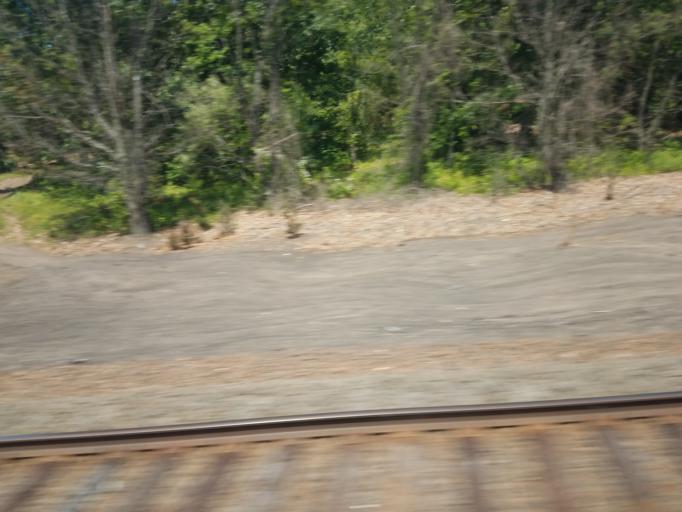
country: US
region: Connecticut
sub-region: New Haven County
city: North Haven
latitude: 41.4042
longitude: -72.8491
